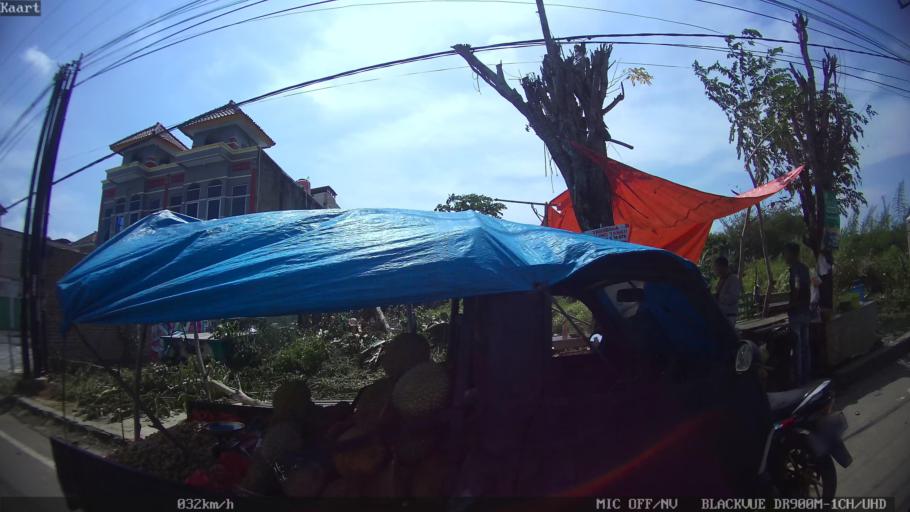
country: ID
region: Lampung
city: Kedaton
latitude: -5.3676
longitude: 105.2561
